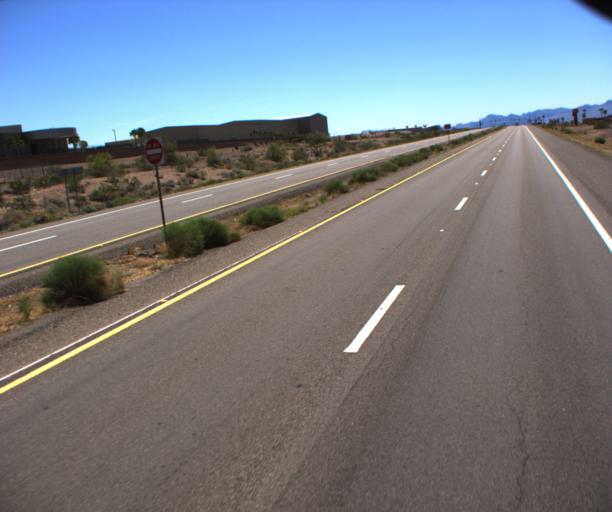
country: US
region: Arizona
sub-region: Mohave County
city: Desert Hills
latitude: 34.5780
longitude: -114.3666
